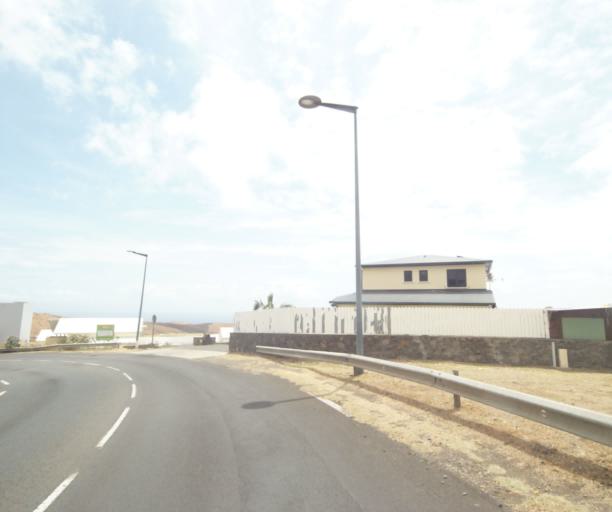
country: RE
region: Reunion
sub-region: Reunion
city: Saint-Paul
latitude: -21.0275
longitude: 55.2682
